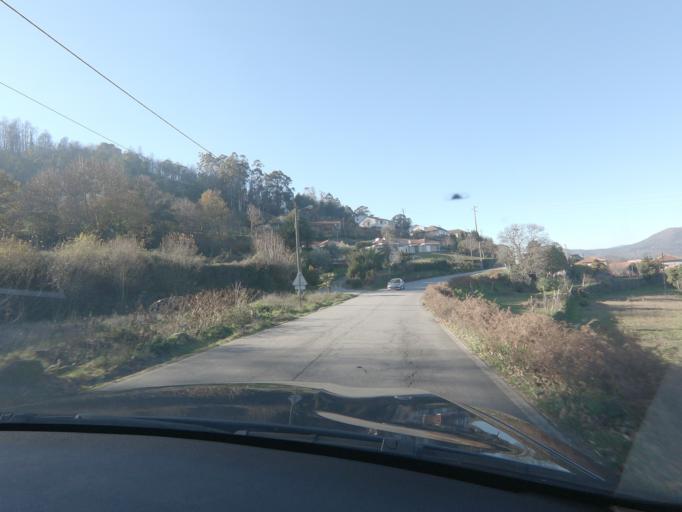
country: PT
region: Viseu
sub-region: Oliveira de Frades
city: Oliveira de Frades
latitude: 40.7304
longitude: -8.1561
